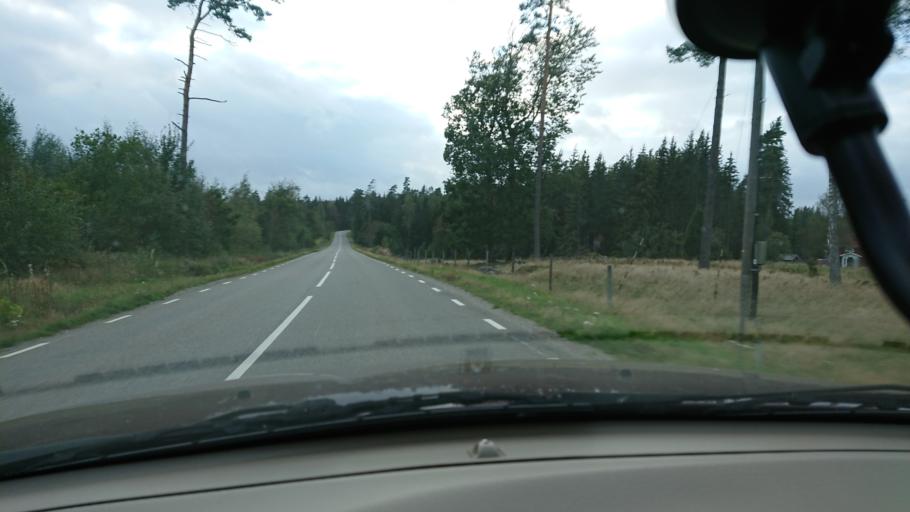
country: SE
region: Kronoberg
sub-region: Vaxjo Kommun
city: Lammhult
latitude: 57.0933
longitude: 14.6917
